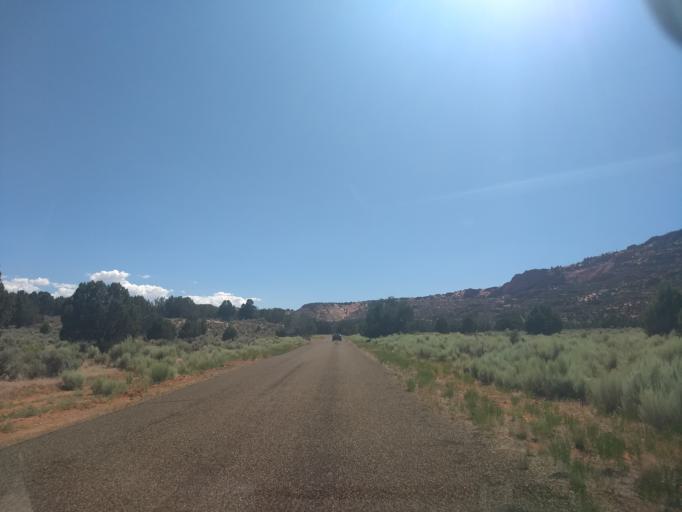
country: US
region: Utah
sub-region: Washington County
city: Hildale
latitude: 37.0058
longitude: -112.8558
